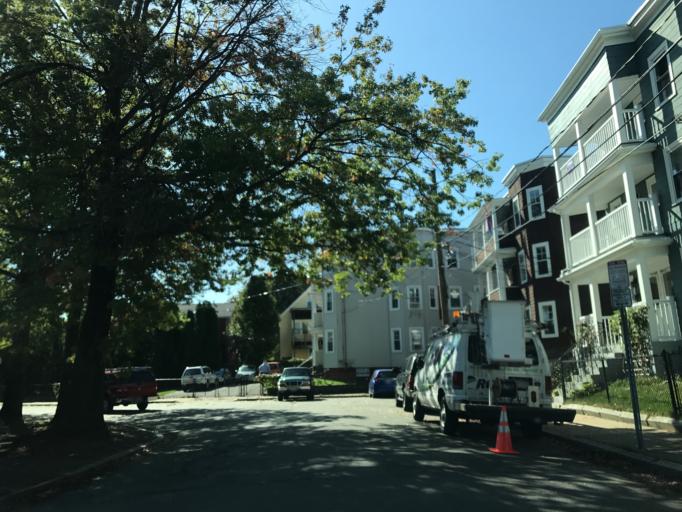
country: US
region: Massachusetts
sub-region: Middlesex County
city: Cambridge
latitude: 42.3782
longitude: -71.1015
